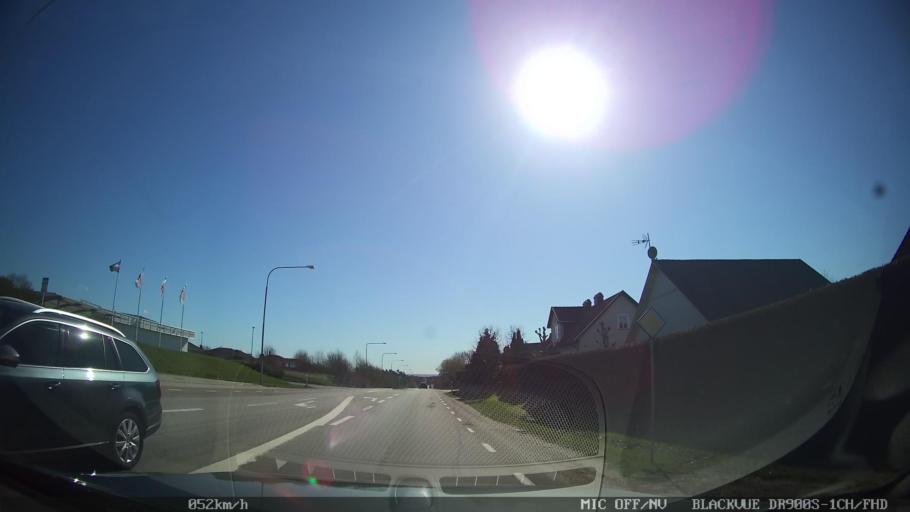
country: SE
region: Skane
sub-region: Ystads Kommun
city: Ystad
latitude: 55.4367
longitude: 13.7955
